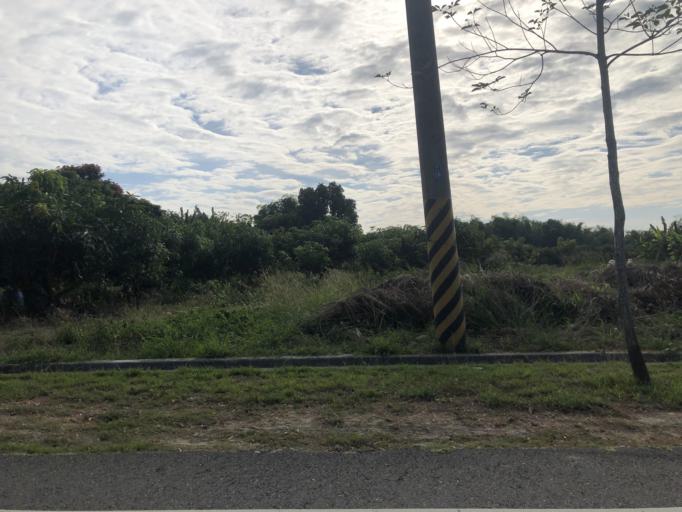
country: TW
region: Taiwan
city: Yujing
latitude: 23.0530
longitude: 120.4161
